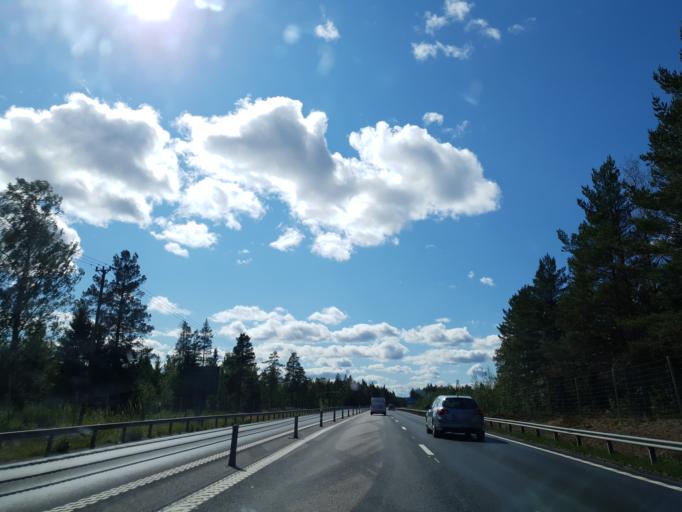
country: SE
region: Vaesterbotten
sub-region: Nordmalings Kommun
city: Nordmaling
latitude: 63.4909
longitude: 19.3144
